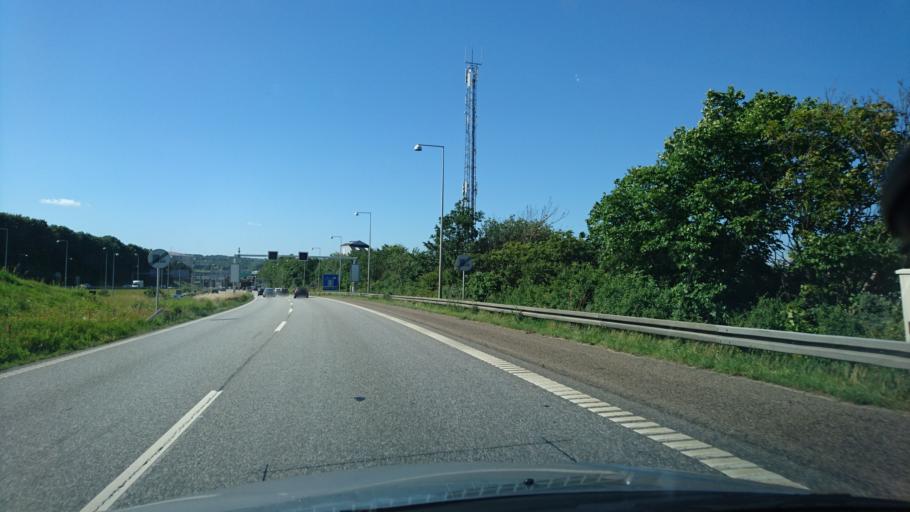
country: DK
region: North Denmark
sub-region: Alborg Kommune
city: Aalborg
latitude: 57.0511
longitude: 9.9690
